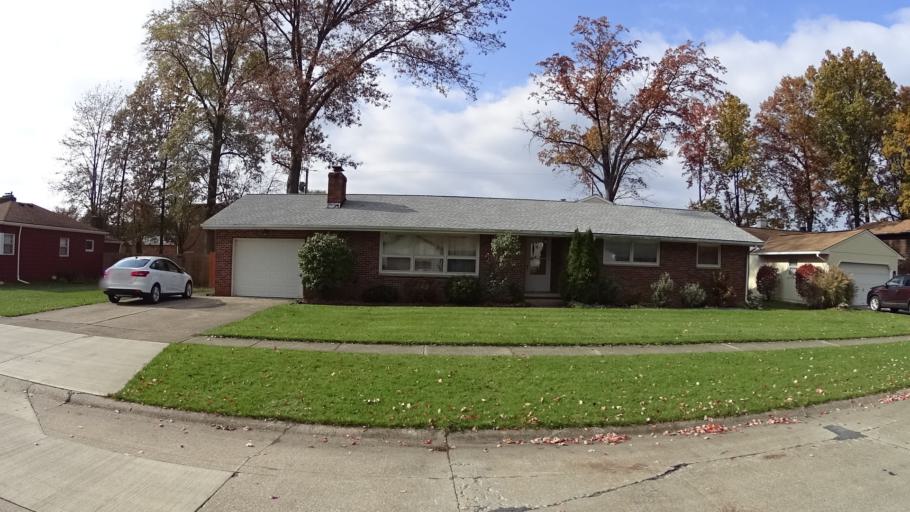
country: US
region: Ohio
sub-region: Lorain County
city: Elyria
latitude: 41.3829
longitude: -82.0836
